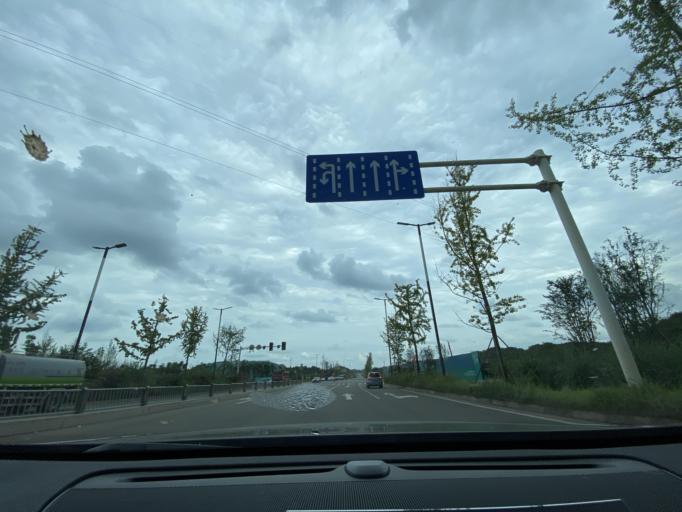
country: CN
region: Sichuan
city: Jiancheng
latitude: 30.4929
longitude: 104.4668
